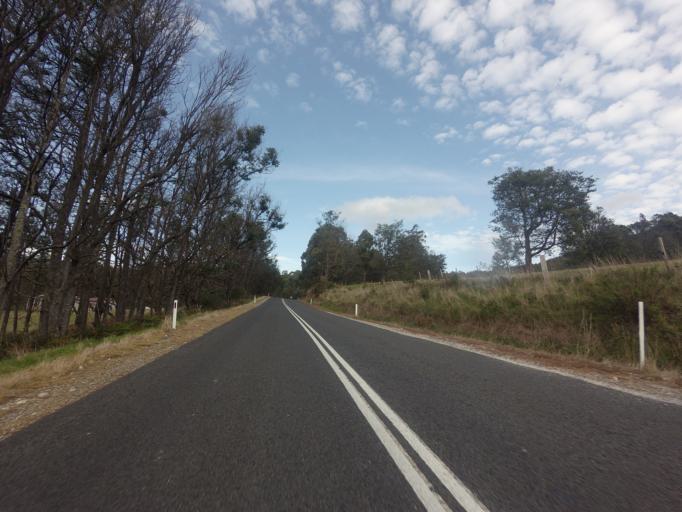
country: AU
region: Tasmania
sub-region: Meander Valley
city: Deloraine
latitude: -41.6359
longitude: 146.7131
